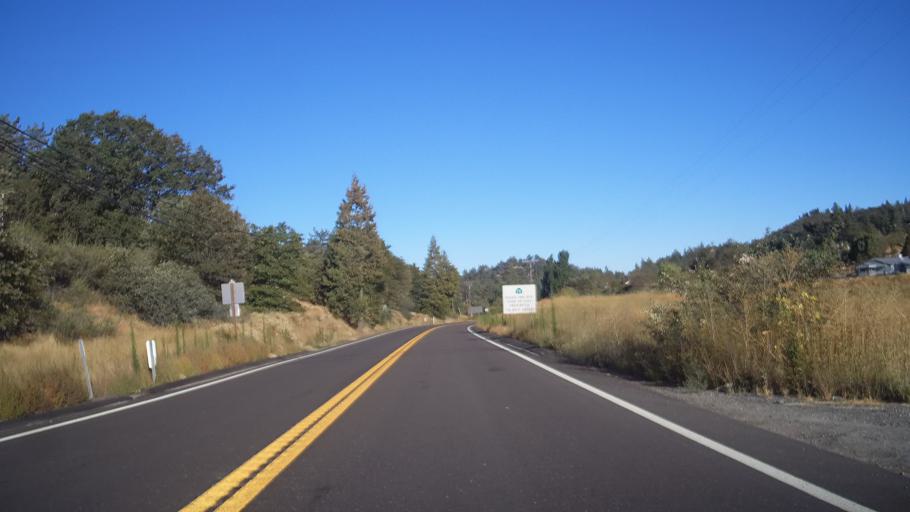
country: US
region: California
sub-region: San Diego County
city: Julian
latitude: 33.0731
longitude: -116.5964
